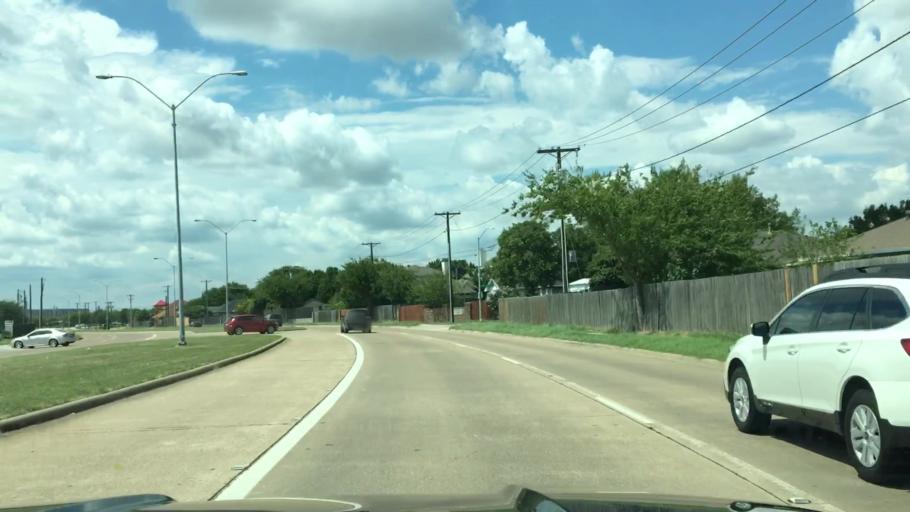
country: US
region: Texas
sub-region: Tarrant County
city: Blue Mound
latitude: 32.8634
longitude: -97.3376
